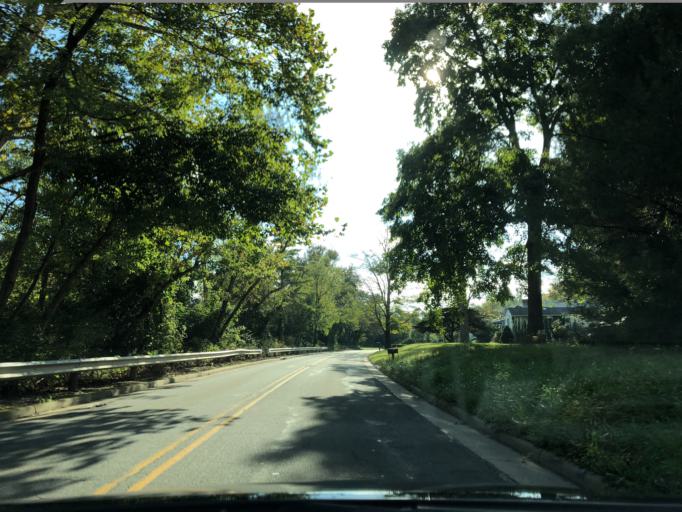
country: US
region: Ohio
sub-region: Hamilton County
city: Loveland
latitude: 39.2596
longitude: -84.2705
